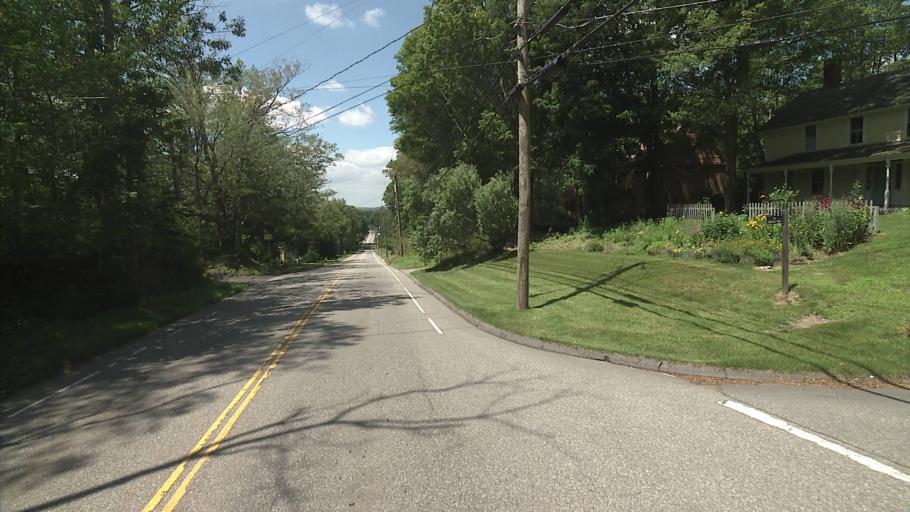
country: US
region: Connecticut
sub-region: Windham County
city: Windham
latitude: 41.7002
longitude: -72.1521
